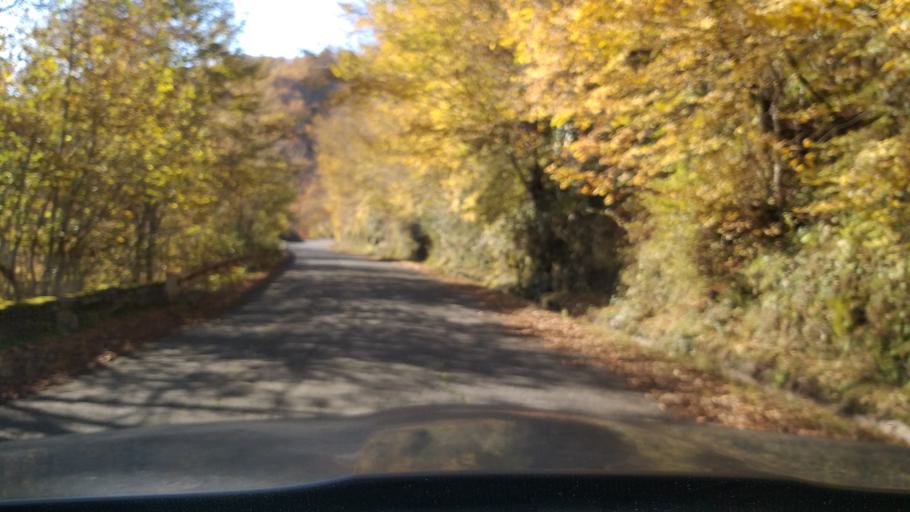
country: GE
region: Abkhazia
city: Bich'vinta
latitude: 43.1910
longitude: 40.4547
